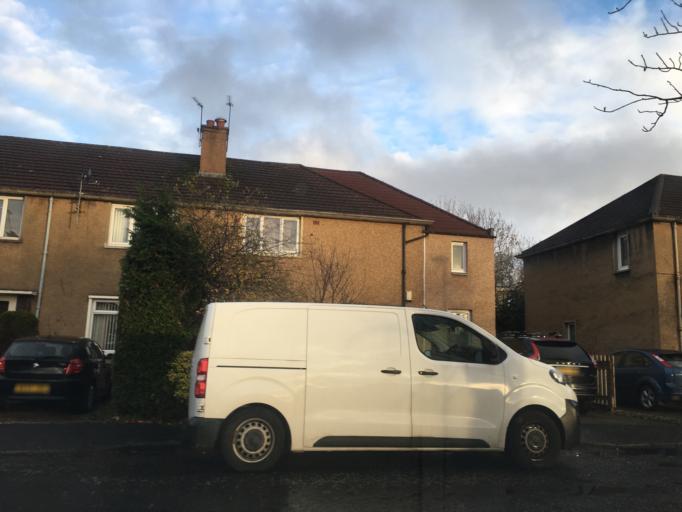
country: GB
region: Scotland
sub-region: Edinburgh
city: Colinton
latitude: 55.9399
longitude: -3.2690
